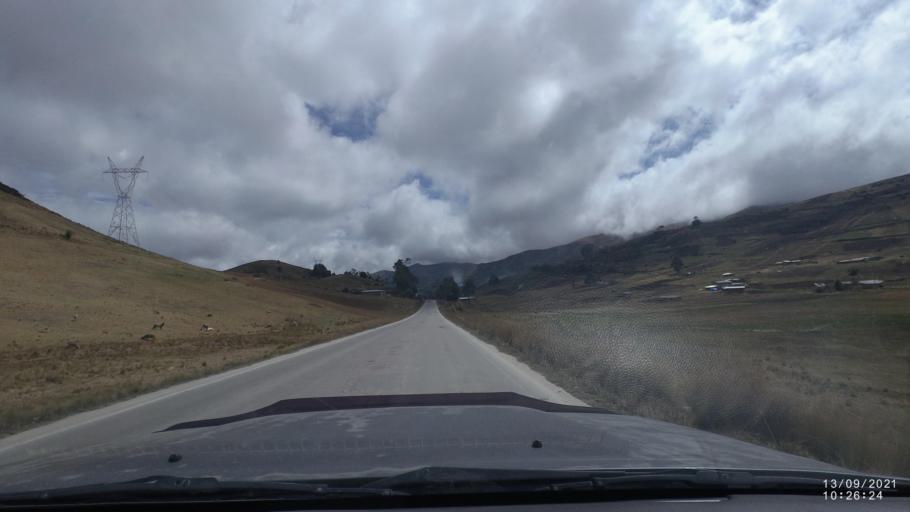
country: BO
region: Cochabamba
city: Colomi
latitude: -17.3017
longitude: -65.8701
